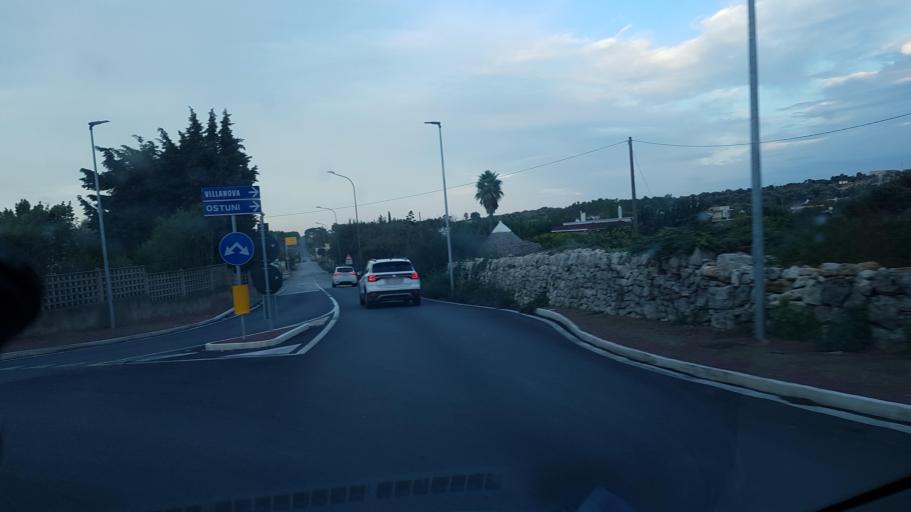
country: IT
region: Apulia
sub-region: Provincia di Brindisi
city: Ceglie Messapica
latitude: 40.6494
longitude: 17.5224
